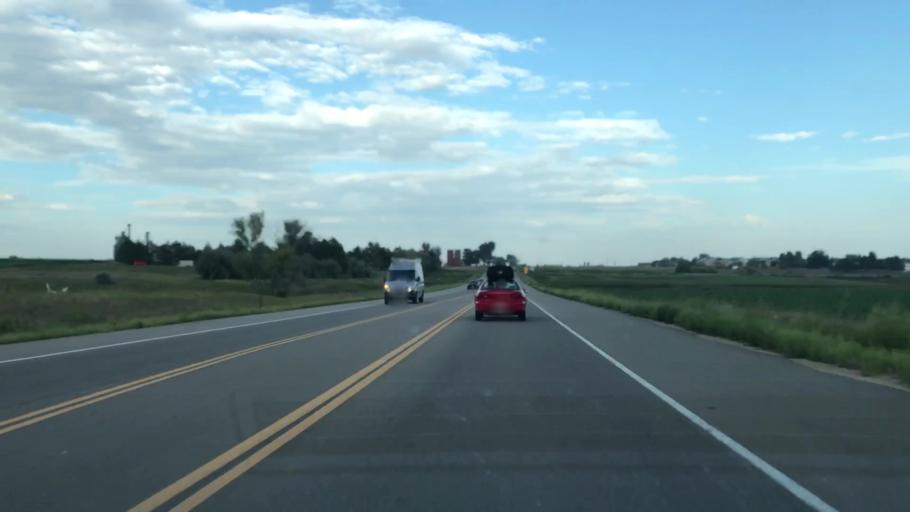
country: US
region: Colorado
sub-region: Weld County
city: Mead
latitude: 40.2039
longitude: -105.0155
